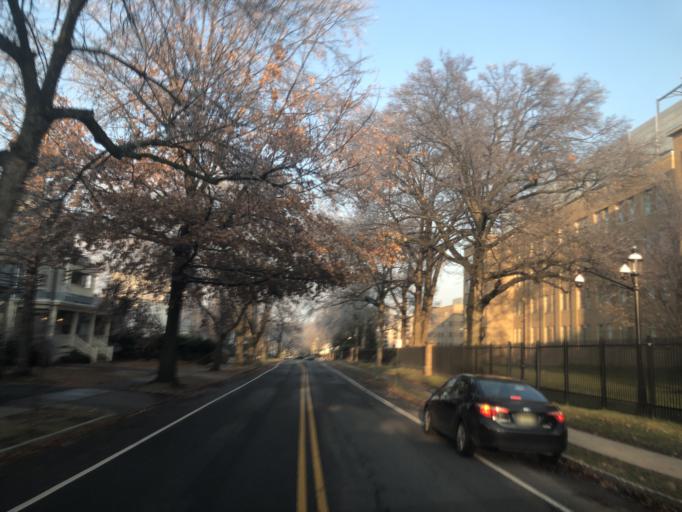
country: US
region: New Jersey
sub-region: Essex County
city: South Orange
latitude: 40.7428
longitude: -74.2503
